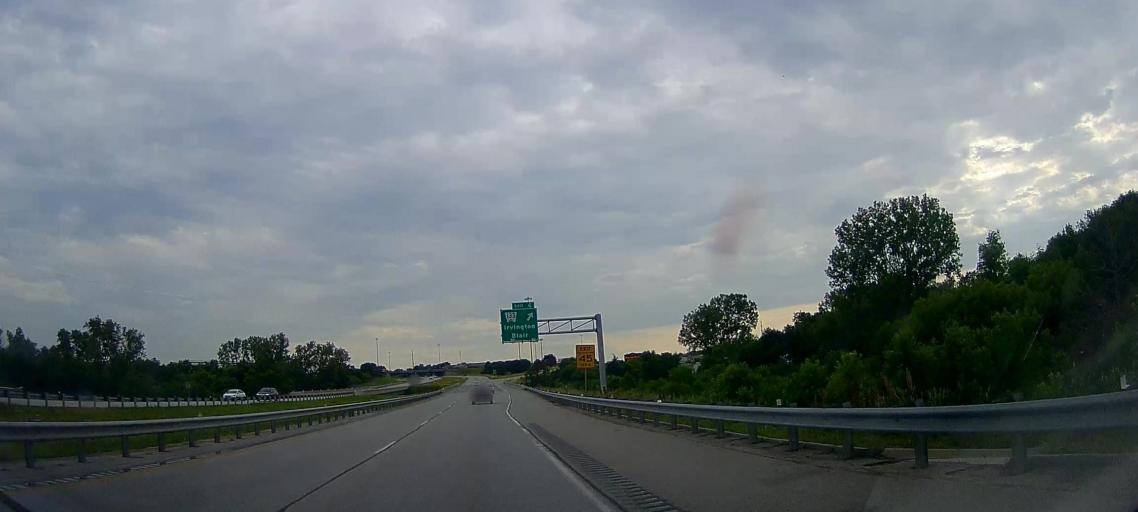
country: US
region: Nebraska
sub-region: Douglas County
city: Bennington
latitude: 41.3267
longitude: -96.0635
